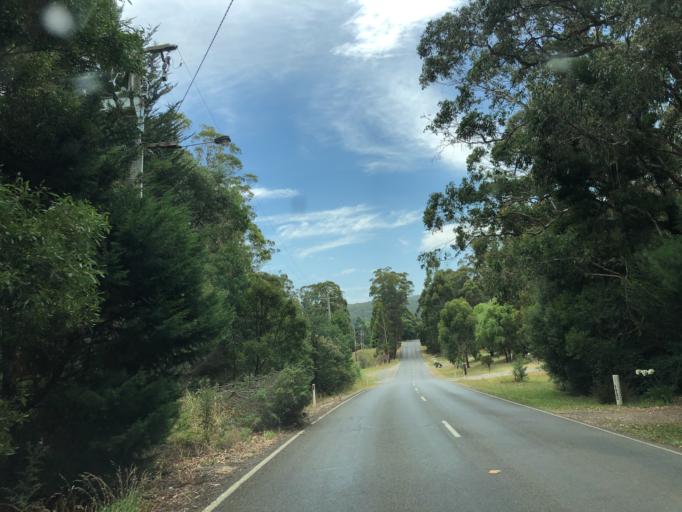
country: AU
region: Victoria
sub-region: Moorabool
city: Bacchus Marsh
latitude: -37.4766
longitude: 144.3052
